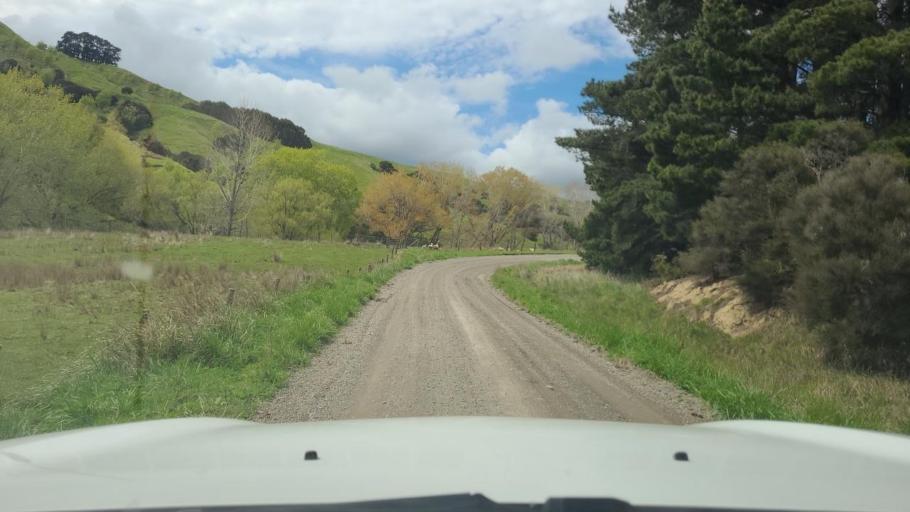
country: NZ
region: Wellington
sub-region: South Wairarapa District
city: Waipawa
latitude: -41.2781
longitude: 175.5544
